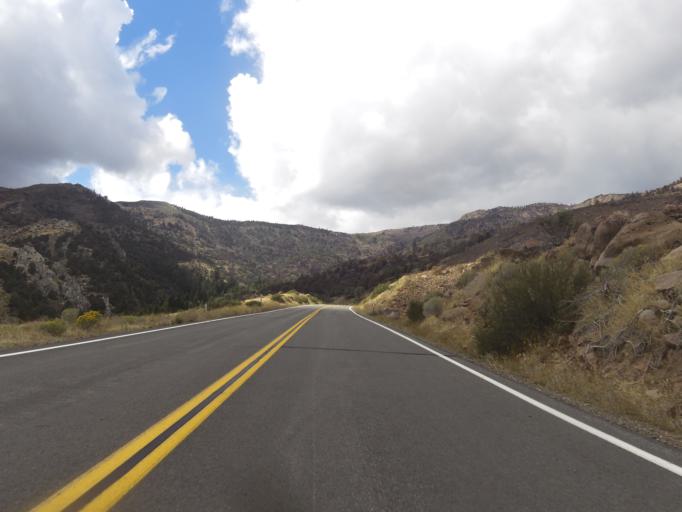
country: US
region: Nevada
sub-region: Lyon County
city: Smith Valley
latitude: 38.6552
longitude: -119.5851
